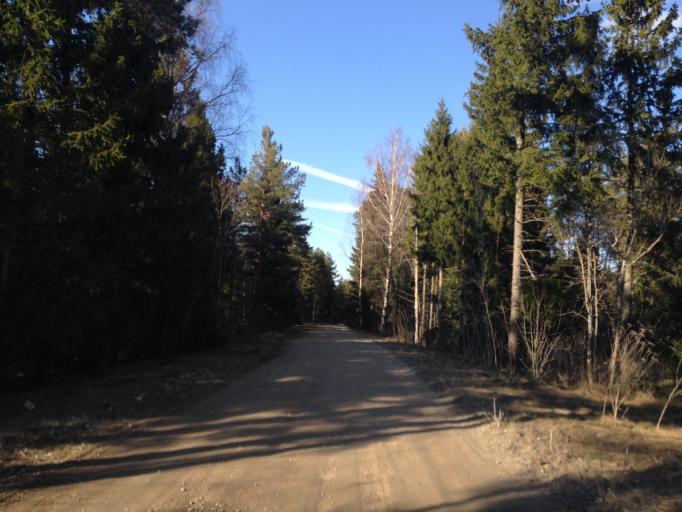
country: EE
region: Harju
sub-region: Nissi vald
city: Turba
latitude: 59.1010
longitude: 24.1535
